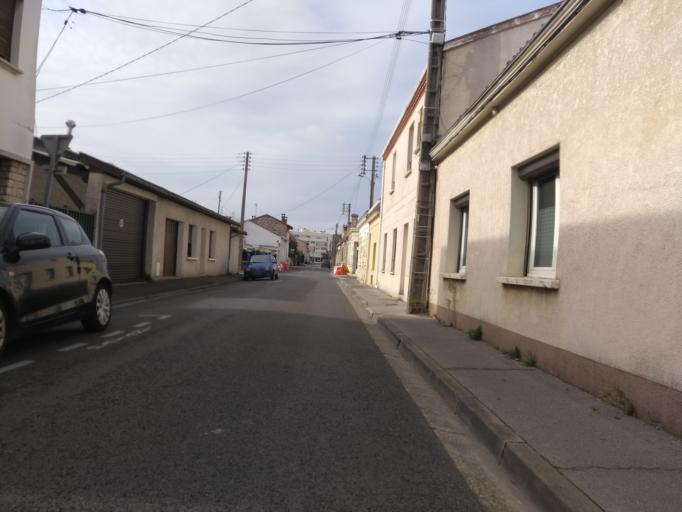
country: FR
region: Aquitaine
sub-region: Departement de la Gironde
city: Talence
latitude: 44.8160
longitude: -0.5894
